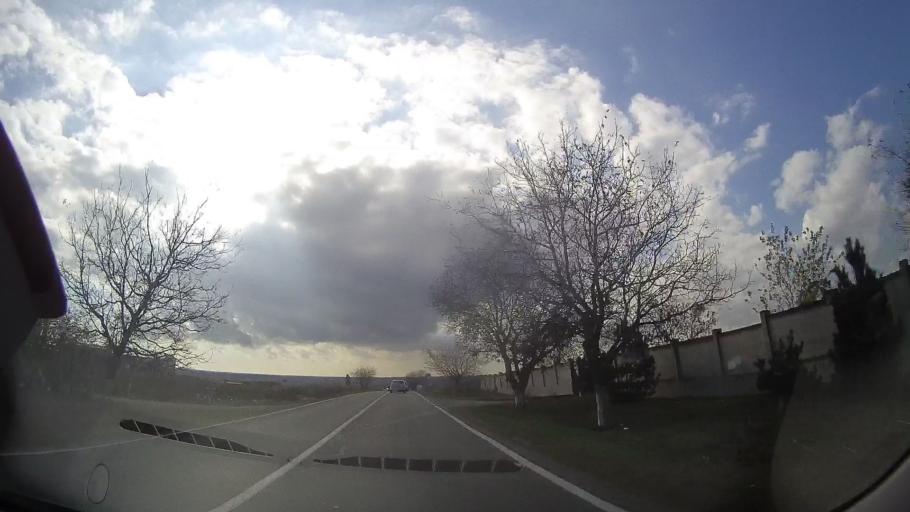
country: RO
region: Constanta
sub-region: Oras Techirghiol
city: Techirghiol
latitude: 44.0712
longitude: 28.5966
